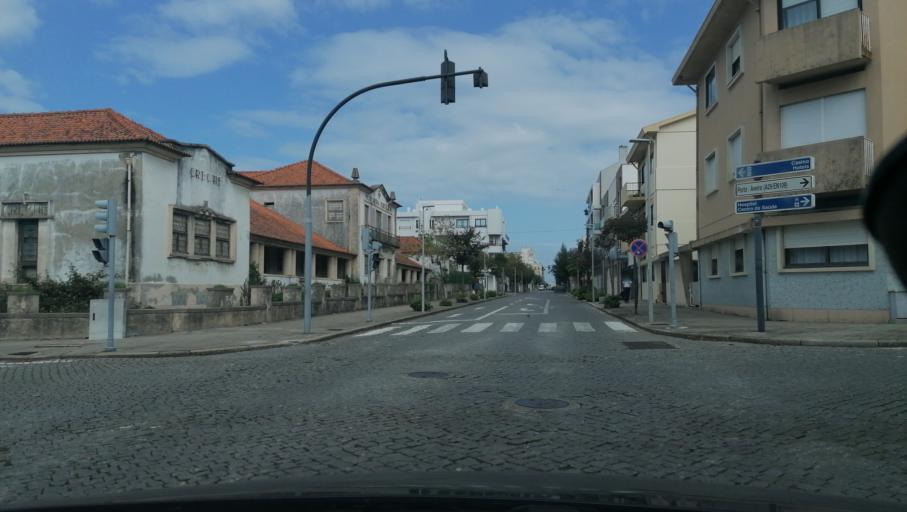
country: PT
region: Aveiro
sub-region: Espinho
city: Espinho
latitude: 41.0022
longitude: -8.6399
